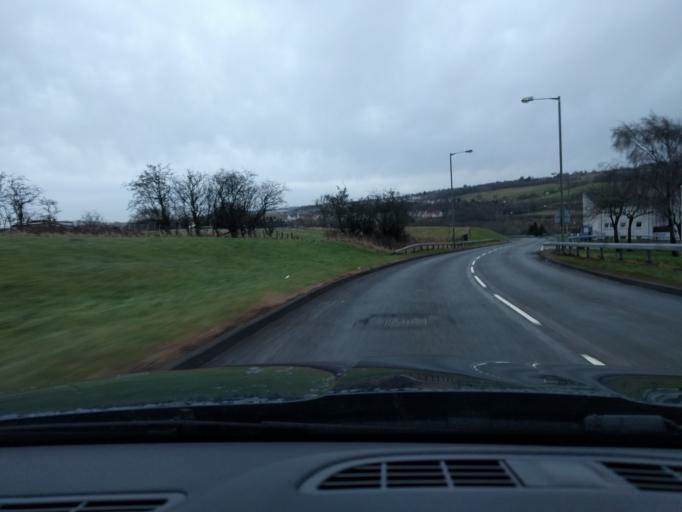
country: GB
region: Scotland
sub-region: Falkirk
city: Falkirk
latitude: 55.9878
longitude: -3.7671
